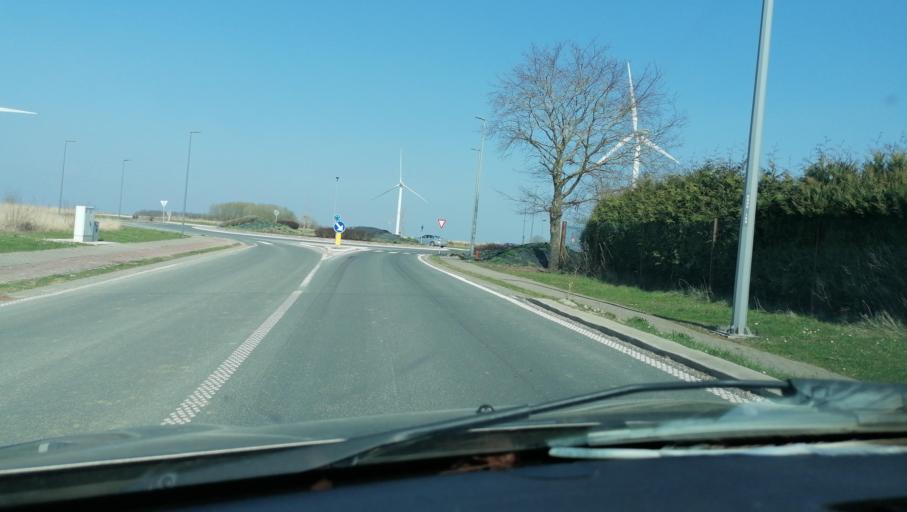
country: BE
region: Wallonia
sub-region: Province du Hainaut
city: Chimay
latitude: 50.0399
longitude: 4.3785
